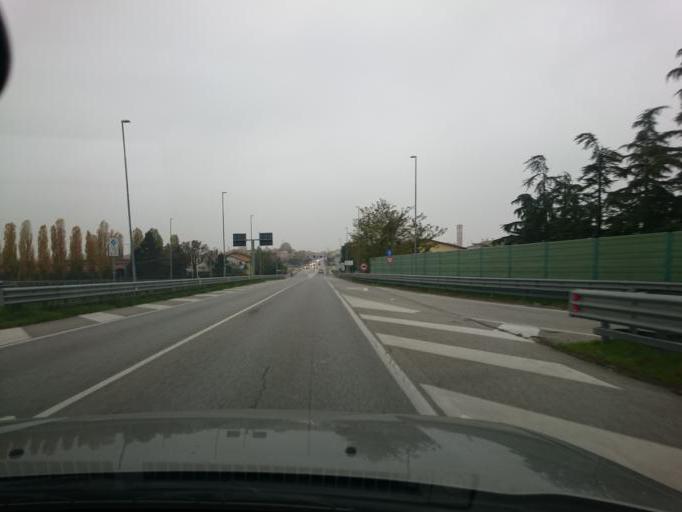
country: IT
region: Veneto
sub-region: Provincia di Padova
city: Ponte San Nicolo
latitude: 45.3598
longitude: 11.9426
